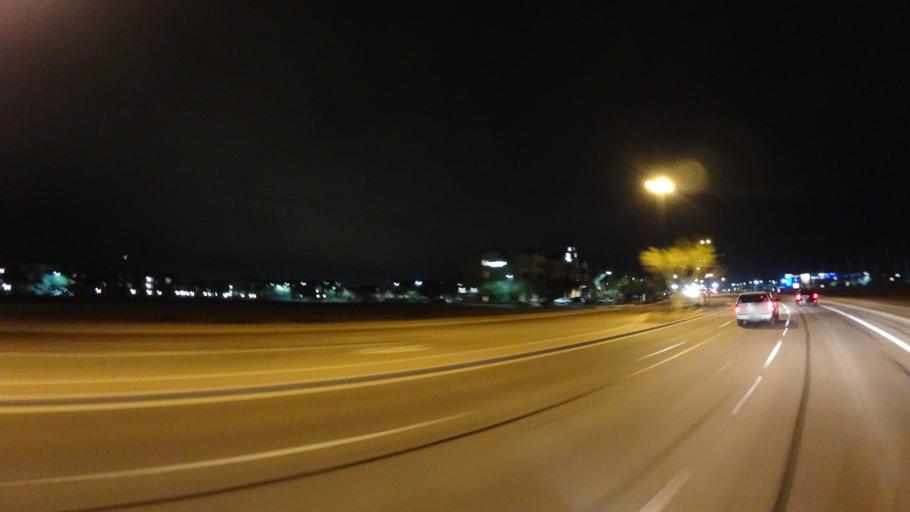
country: US
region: Arizona
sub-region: Maricopa County
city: Gilbert
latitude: 33.3157
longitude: -111.7430
